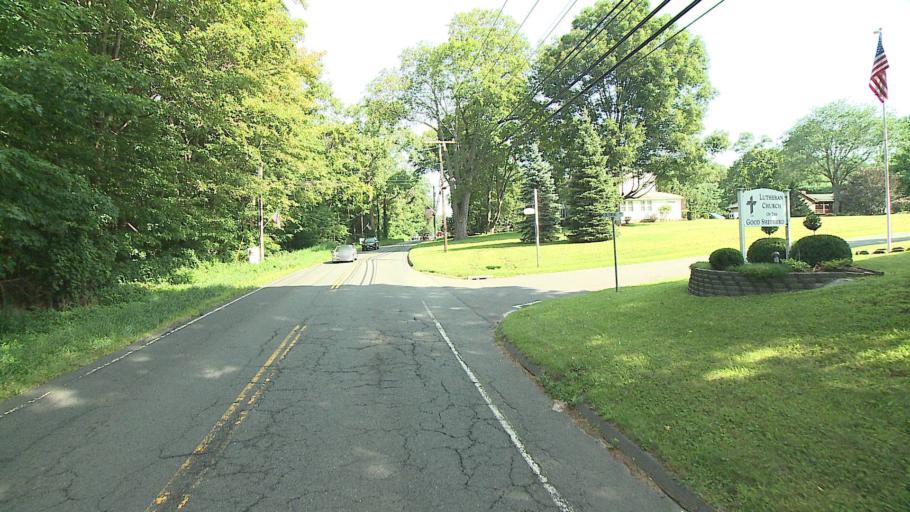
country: US
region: New York
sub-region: Putnam County
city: Putnam Lake
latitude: 41.4611
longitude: -73.4805
